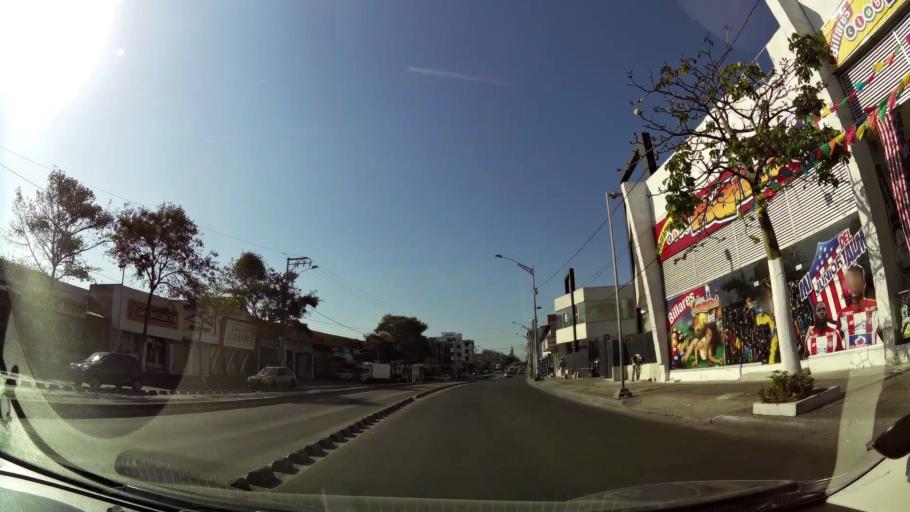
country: CO
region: Atlantico
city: Barranquilla
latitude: 10.9810
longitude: -74.7868
